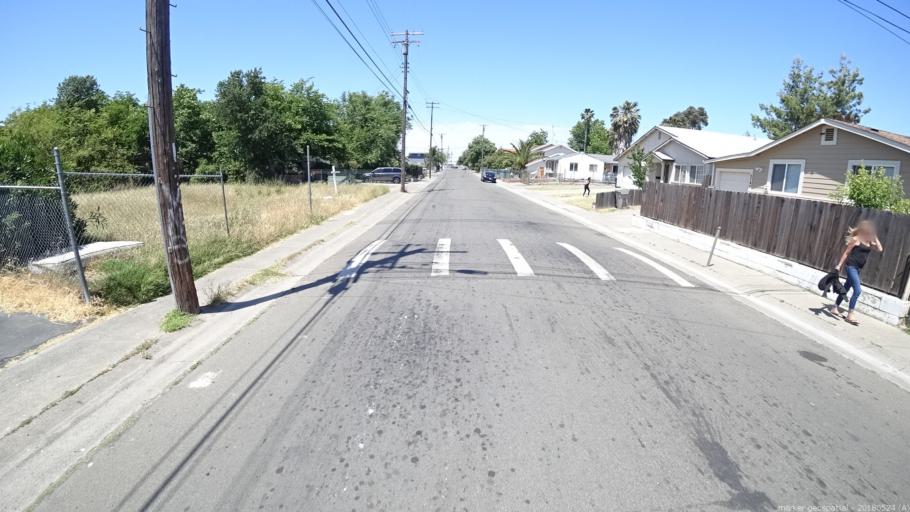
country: US
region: California
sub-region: Sacramento County
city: Sacramento
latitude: 38.6181
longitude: -121.4527
